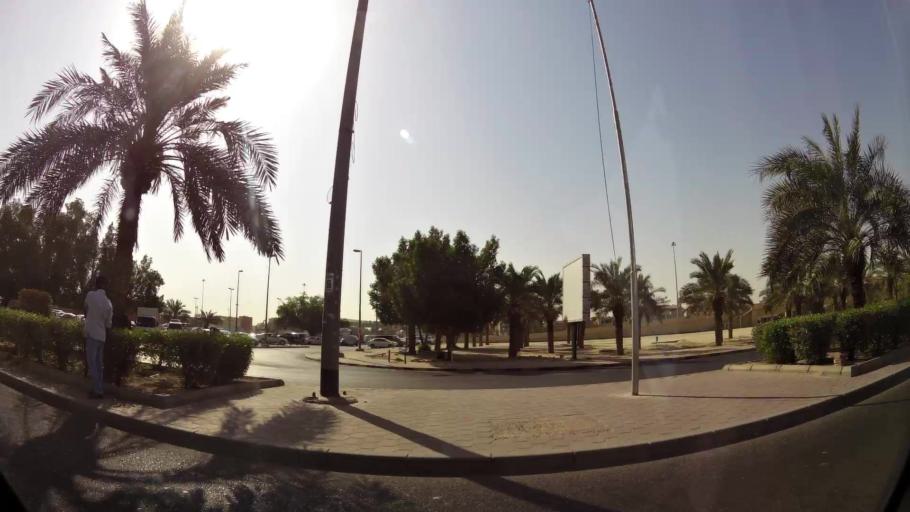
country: KW
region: Al Asimah
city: Ash Shamiyah
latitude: 29.3608
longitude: 47.9653
